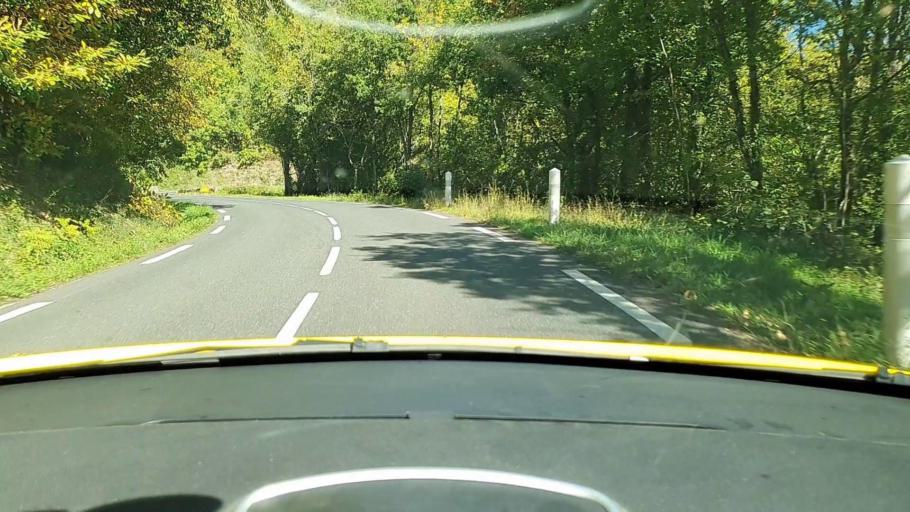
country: FR
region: Languedoc-Roussillon
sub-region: Departement du Gard
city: Le Vigan
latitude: 43.9706
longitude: 3.4080
